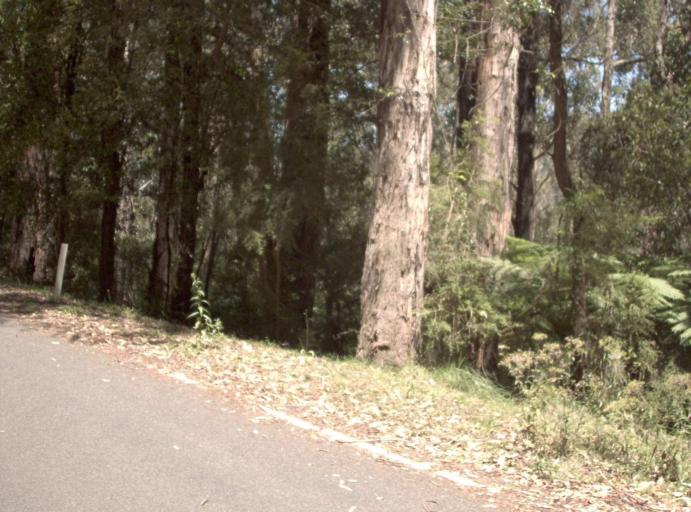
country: AU
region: Victoria
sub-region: Yarra Ranges
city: Millgrove
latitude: -37.7415
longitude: 145.7167
